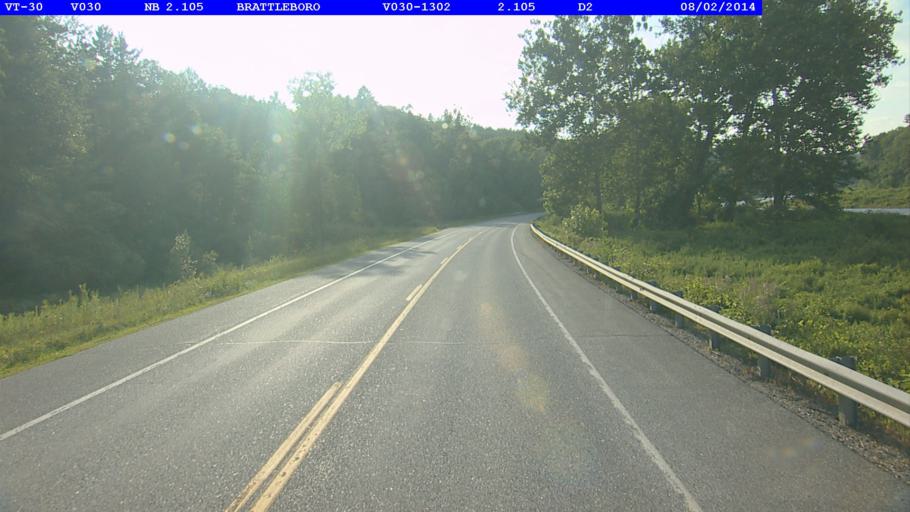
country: US
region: Vermont
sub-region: Windham County
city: West Brattleboro
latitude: 42.8811
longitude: -72.5829
